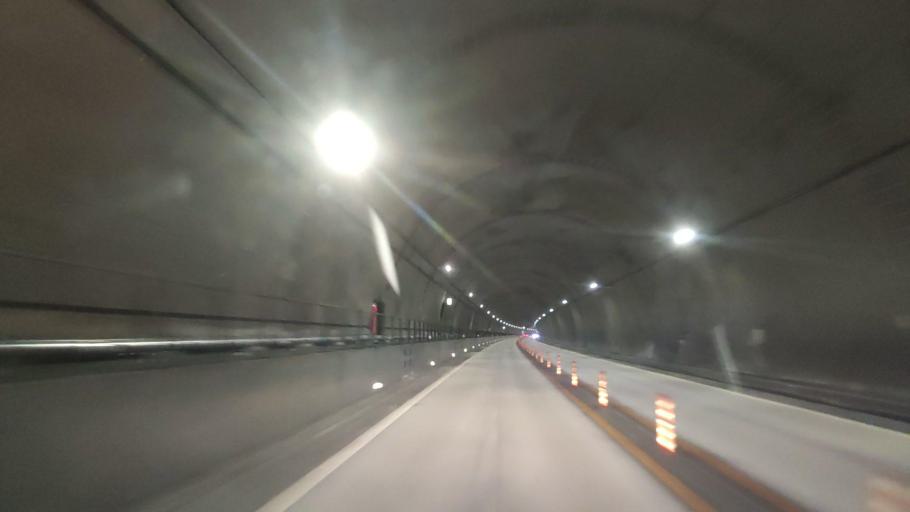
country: JP
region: Ehime
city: Hojo
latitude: 34.0799
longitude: 132.9764
